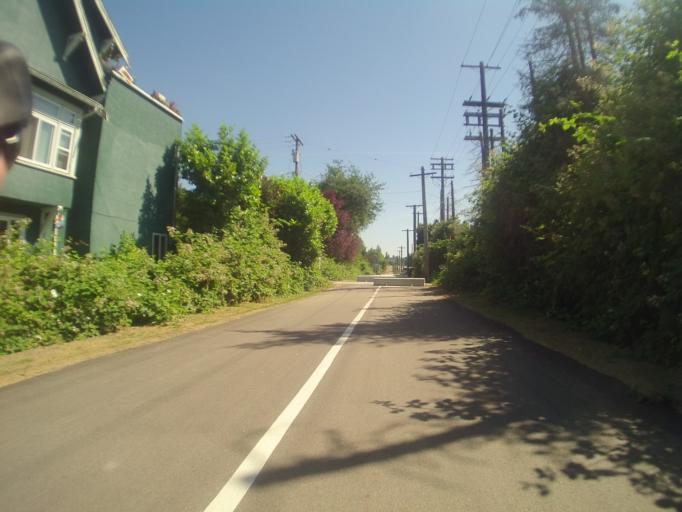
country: CA
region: British Columbia
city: West End
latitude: 49.2580
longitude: -123.1527
